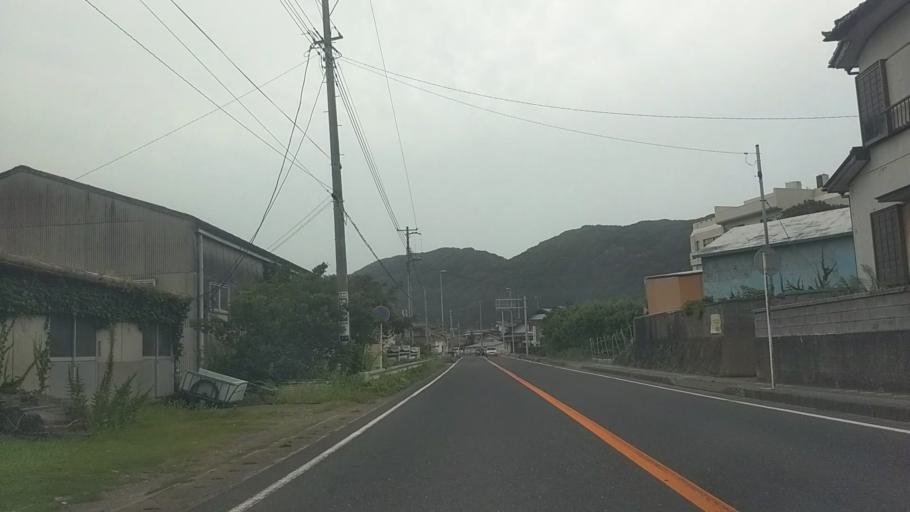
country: JP
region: Chiba
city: Futtsu
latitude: 35.1652
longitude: 139.8226
